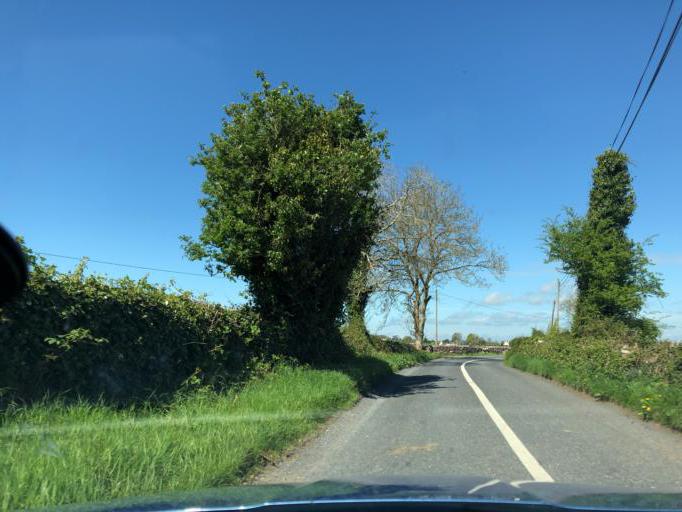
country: IE
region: Connaught
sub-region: County Galway
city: Loughrea
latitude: 53.1641
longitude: -8.4058
